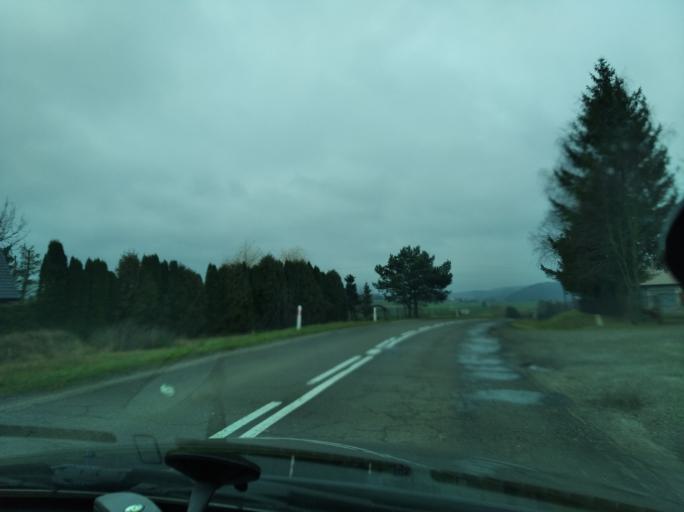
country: PL
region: Subcarpathian Voivodeship
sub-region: Powiat rzeszowski
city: Dynow
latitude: 49.8455
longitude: 22.2437
